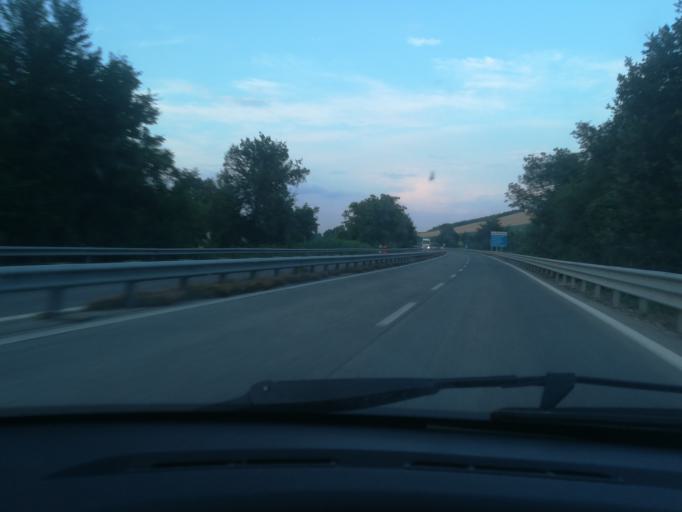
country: IT
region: The Marches
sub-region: Provincia di Macerata
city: Casette Verdini
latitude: 43.2377
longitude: 13.4035
